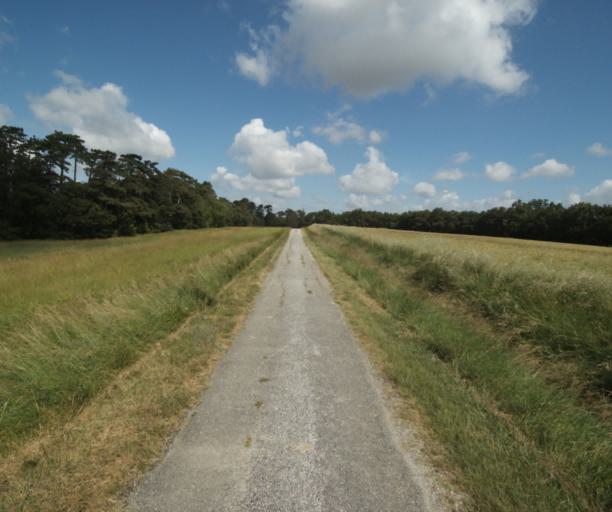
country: FR
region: Midi-Pyrenees
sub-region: Departement de la Haute-Garonne
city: Saint-Felix-Lauragais
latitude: 43.4286
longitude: 1.9290
